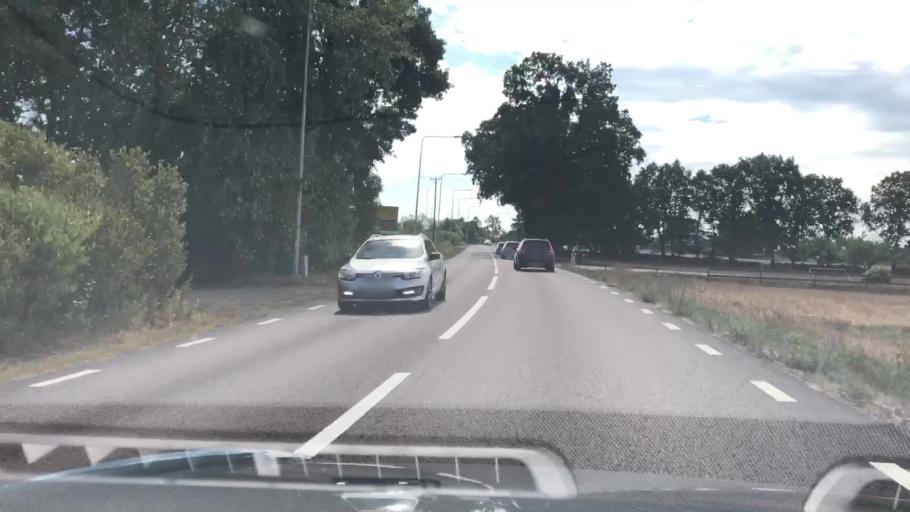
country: SE
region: Kalmar
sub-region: Torsas Kommun
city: Torsas
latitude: 56.3814
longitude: 16.0692
